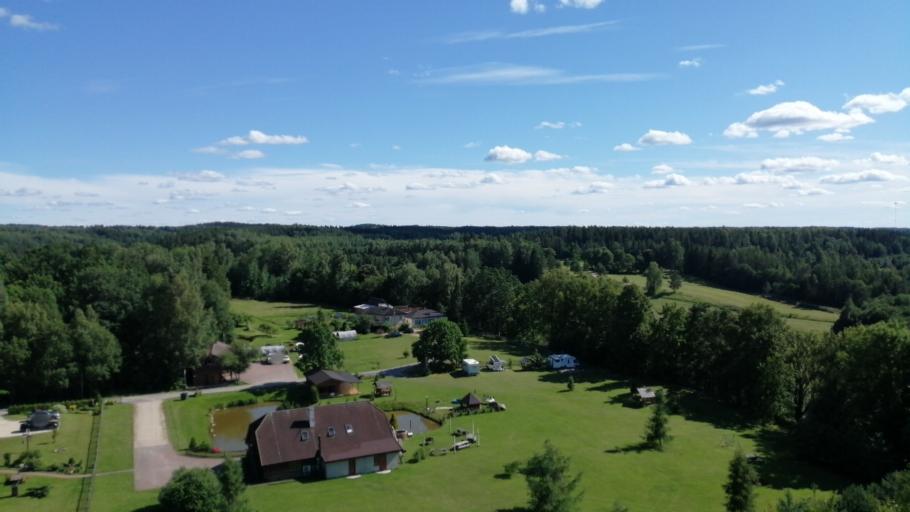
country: EE
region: Vorumaa
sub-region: Voru linn
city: Voru
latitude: 57.7277
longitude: 26.9374
